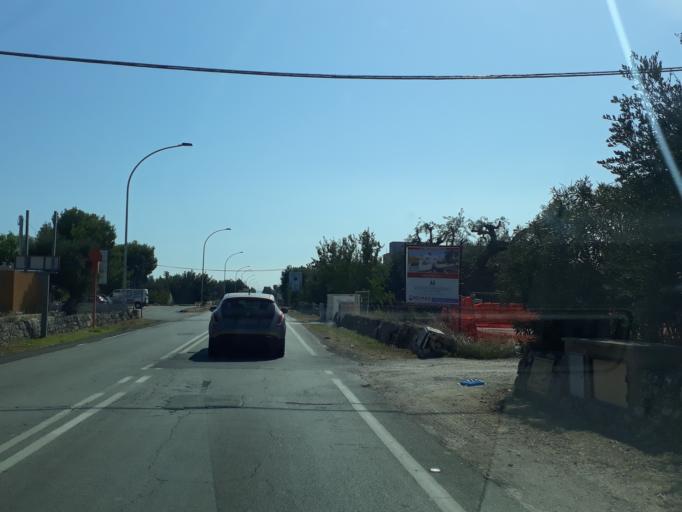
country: IT
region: Apulia
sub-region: Provincia di Bari
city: Monopoli
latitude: 40.9369
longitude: 17.3086
